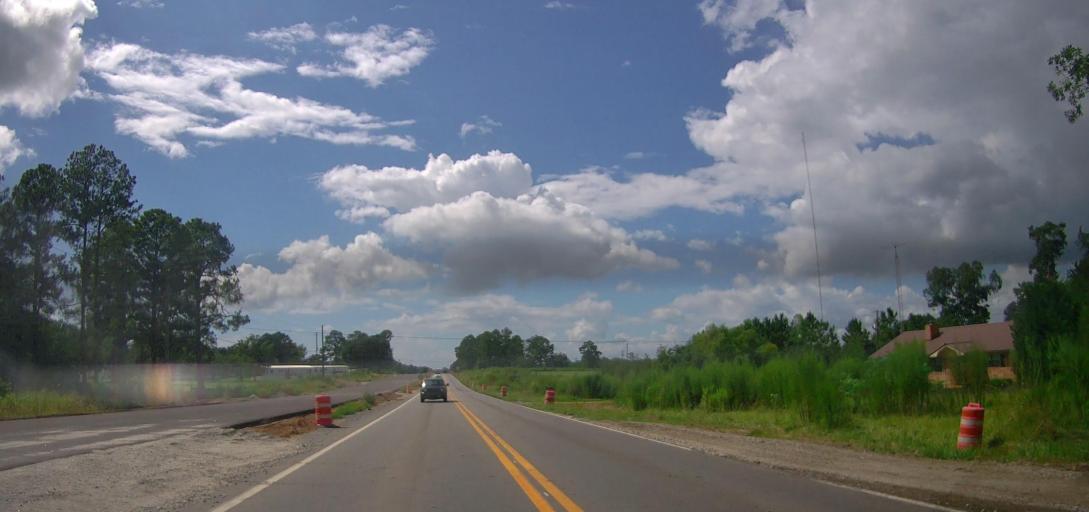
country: US
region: Georgia
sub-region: Coffee County
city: Douglas
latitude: 31.5287
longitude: -82.9081
